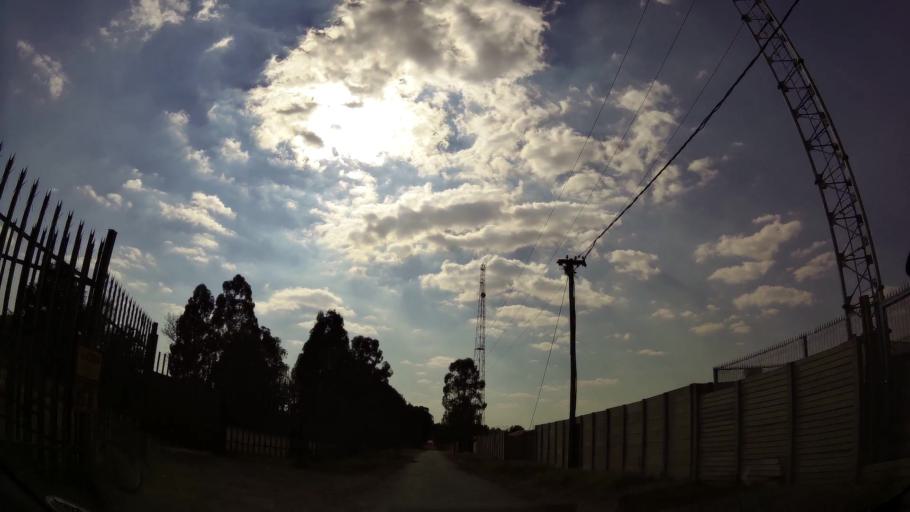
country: ZA
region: Gauteng
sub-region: Ekurhuleni Metropolitan Municipality
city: Benoni
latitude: -26.0883
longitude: 28.3654
